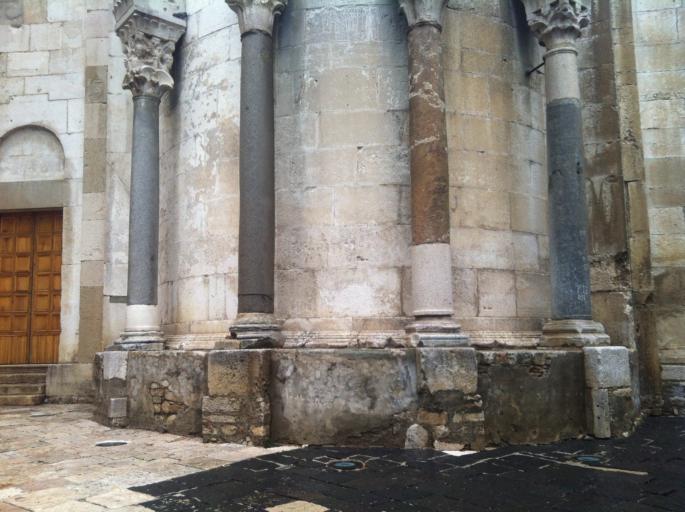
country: IT
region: Apulia
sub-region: Provincia di Foggia
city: Troia
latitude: 41.3608
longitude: 15.3087
